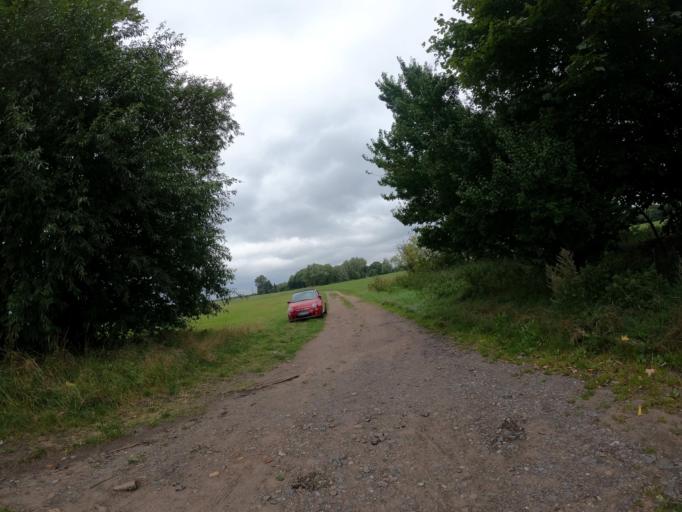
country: DE
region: Mecklenburg-Vorpommern
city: Altefahr
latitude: 54.3203
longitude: 13.1519
